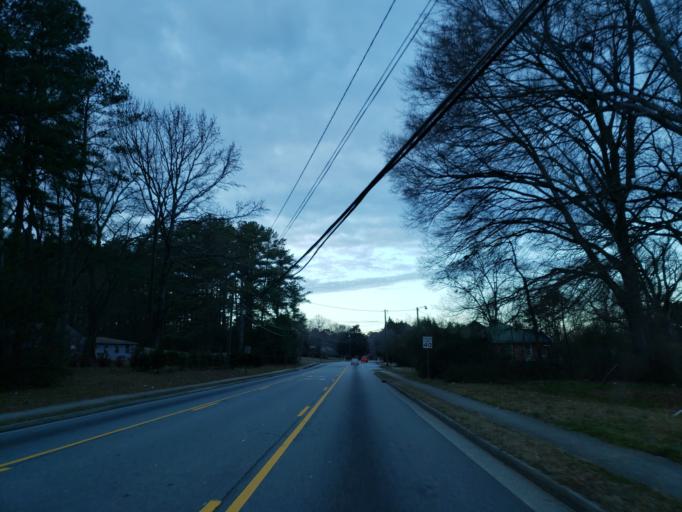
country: US
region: Georgia
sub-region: Cobb County
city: Mableton
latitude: 33.8490
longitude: -84.5866
